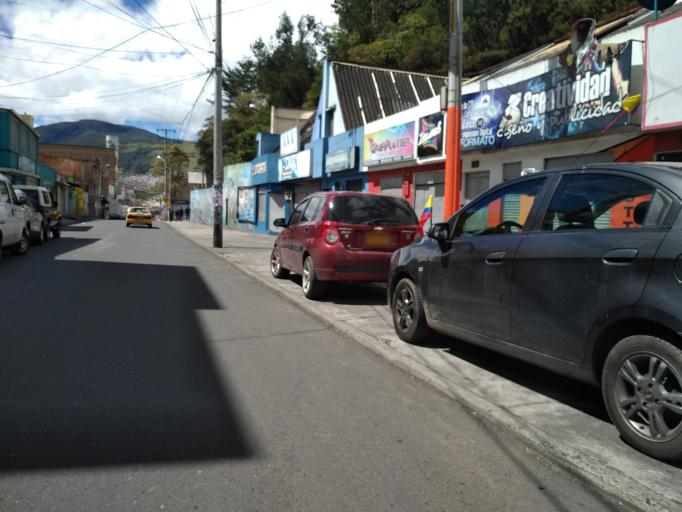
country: CO
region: Narino
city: Pasto
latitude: 1.2089
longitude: -77.2797
